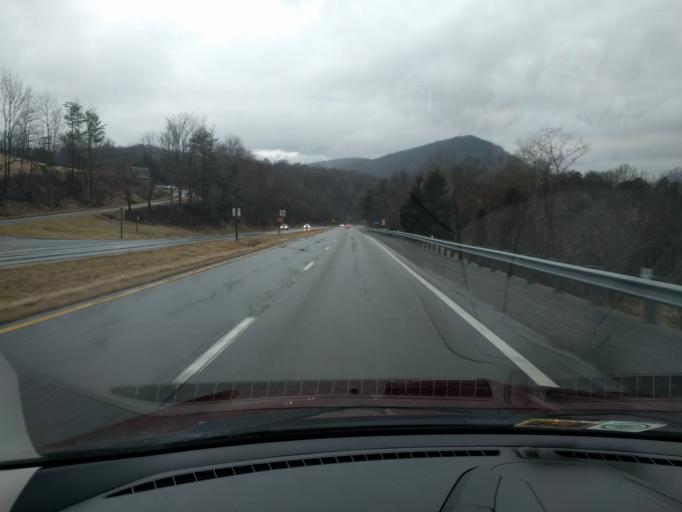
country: US
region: Virginia
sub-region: Montgomery County
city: Prices Fork
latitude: 37.2874
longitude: -80.4897
